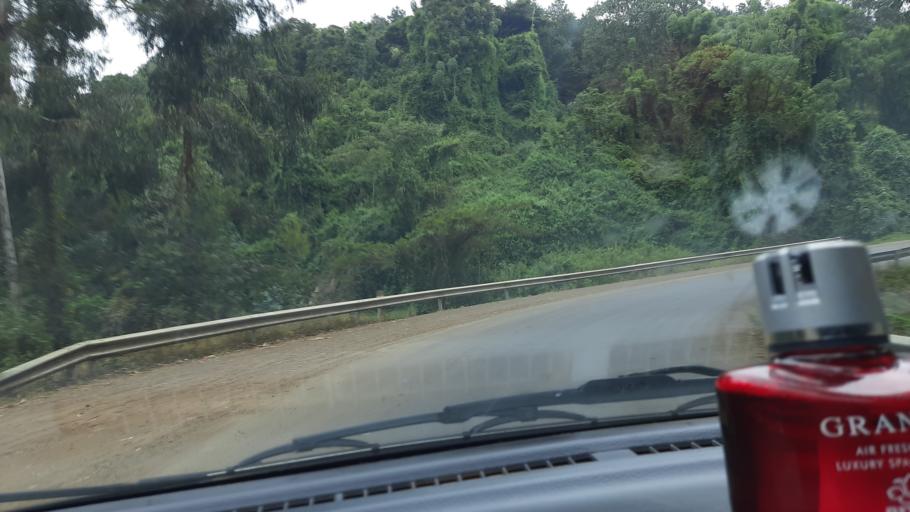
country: TZ
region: Kilimanjaro
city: Moshi
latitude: -2.9687
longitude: 37.5082
